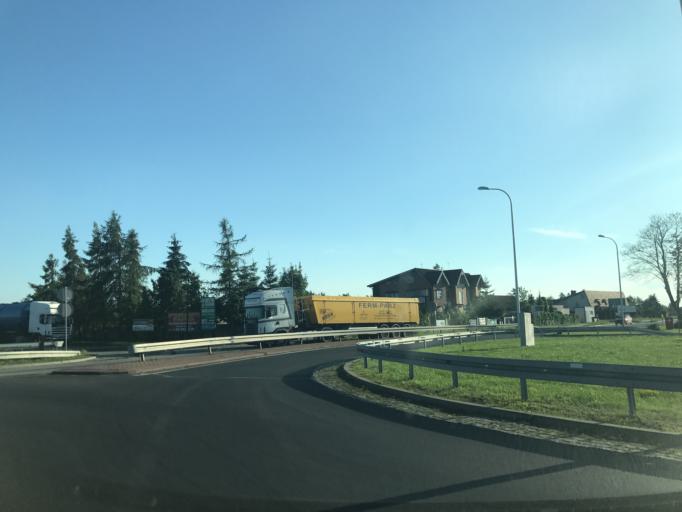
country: PL
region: Greater Poland Voivodeship
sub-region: Powiat koninski
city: Rychwal
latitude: 52.0678
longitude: 18.1620
